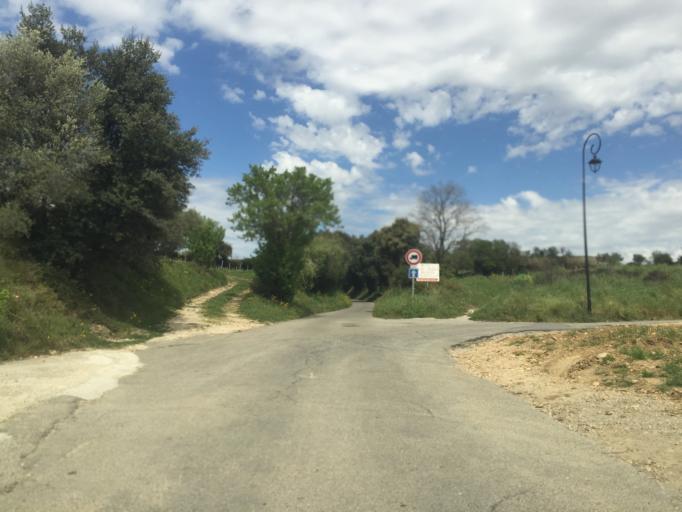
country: FR
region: Provence-Alpes-Cote d'Azur
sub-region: Departement du Vaucluse
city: Chateauneuf-du-Pape
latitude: 44.0623
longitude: 4.8333
